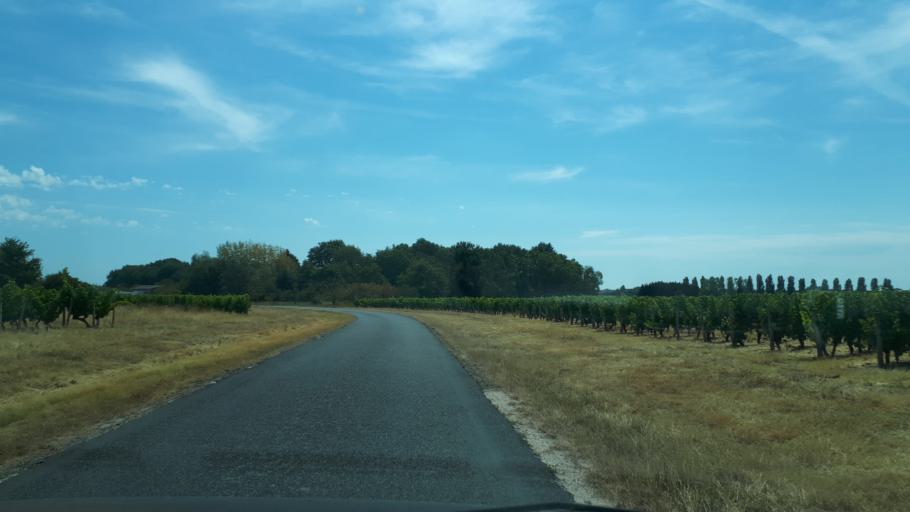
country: FR
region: Centre
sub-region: Departement du Loir-et-Cher
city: Contres
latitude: 47.3998
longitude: 1.3741
